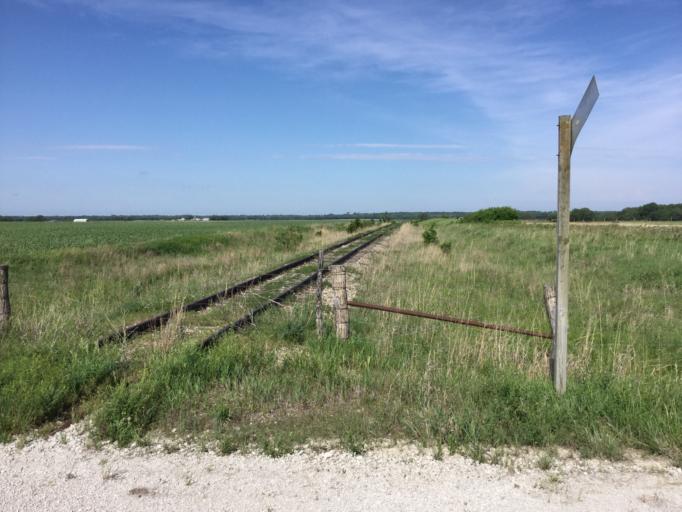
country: US
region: Kansas
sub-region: Coffey County
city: Burlington
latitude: 38.1766
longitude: -95.6102
